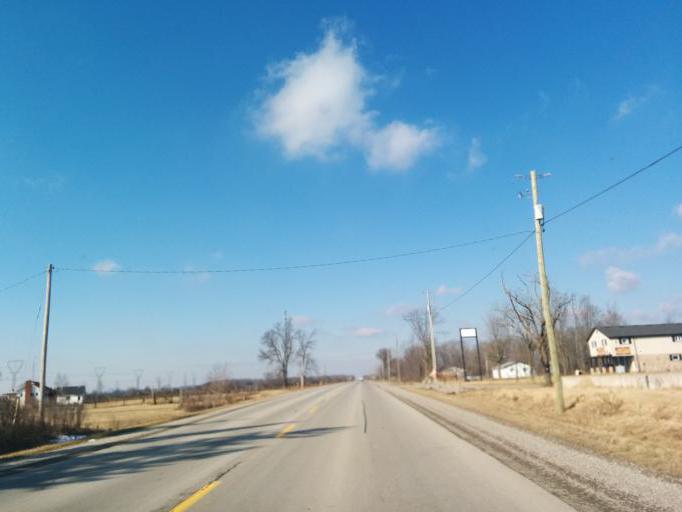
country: CA
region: Ontario
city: Brantford
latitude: 43.0053
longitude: -80.1691
